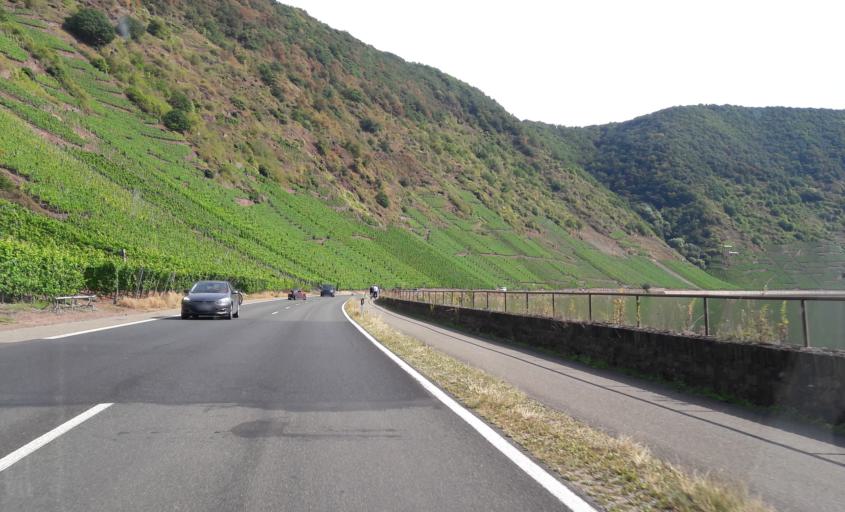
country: DE
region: Rheinland-Pfalz
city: Mesenich
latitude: 50.1110
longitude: 7.1950
